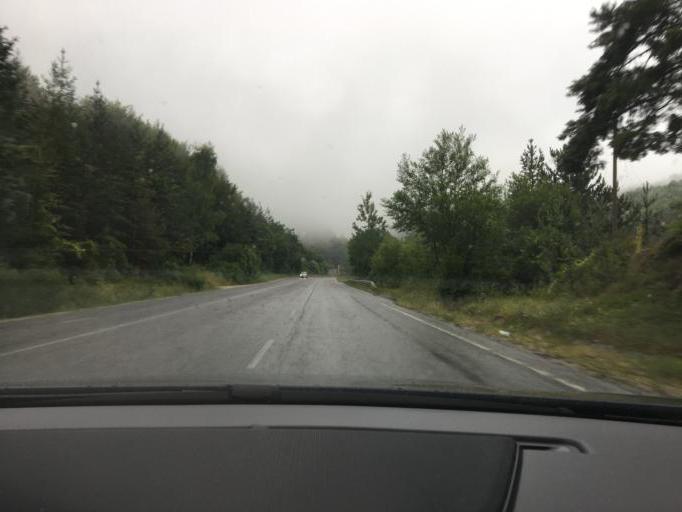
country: MK
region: Kriva Palanka
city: Kriva Palanka
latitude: 42.2189
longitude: 22.4723
